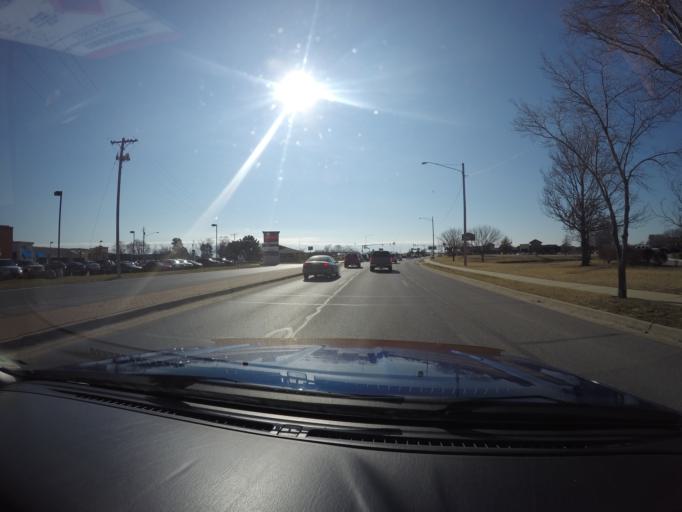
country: US
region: Kansas
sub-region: Sedgwick County
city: Wichita
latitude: 37.6779
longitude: -97.4262
